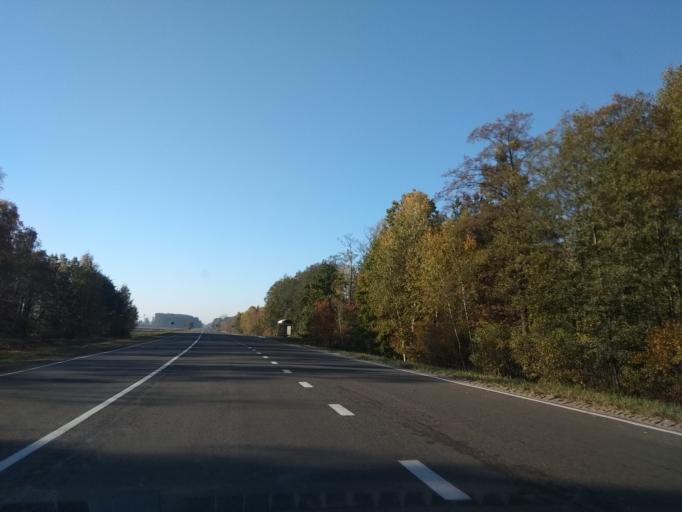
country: BY
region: Brest
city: Kobryn
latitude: 52.0072
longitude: 24.2173
